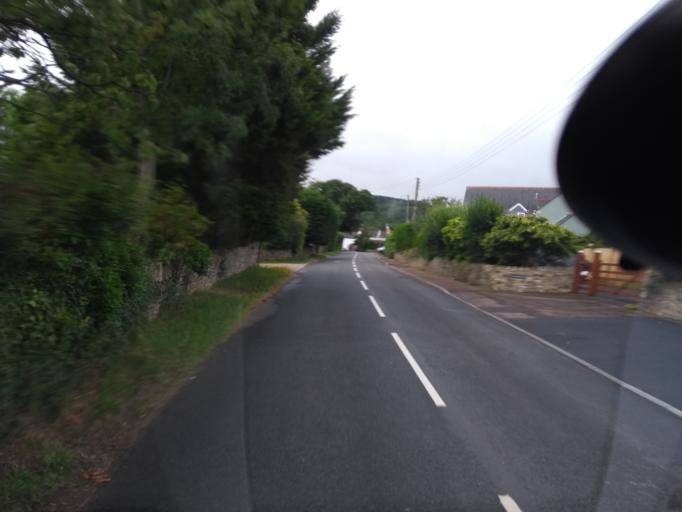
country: GB
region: England
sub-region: Somerset
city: Taunton
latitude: 50.9620
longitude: -3.1242
